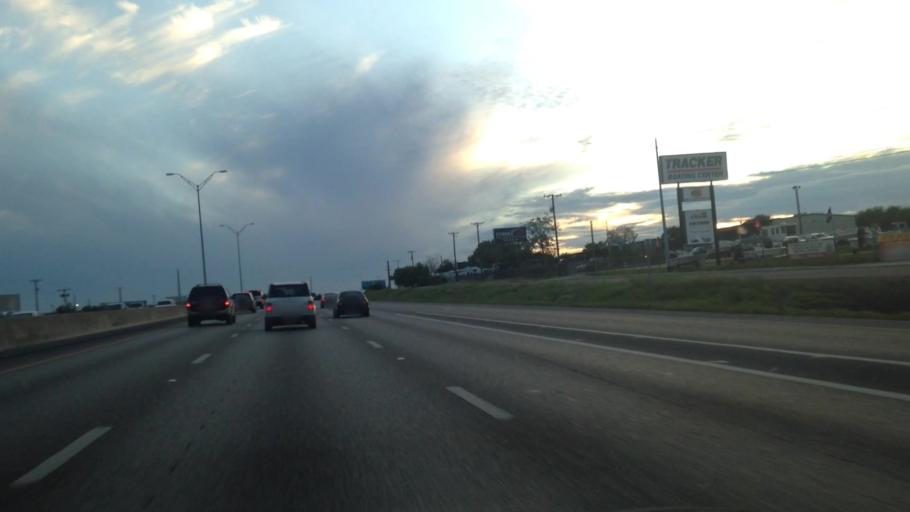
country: US
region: Texas
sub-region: Guadalupe County
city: Northcliff
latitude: 29.6498
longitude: -98.1952
